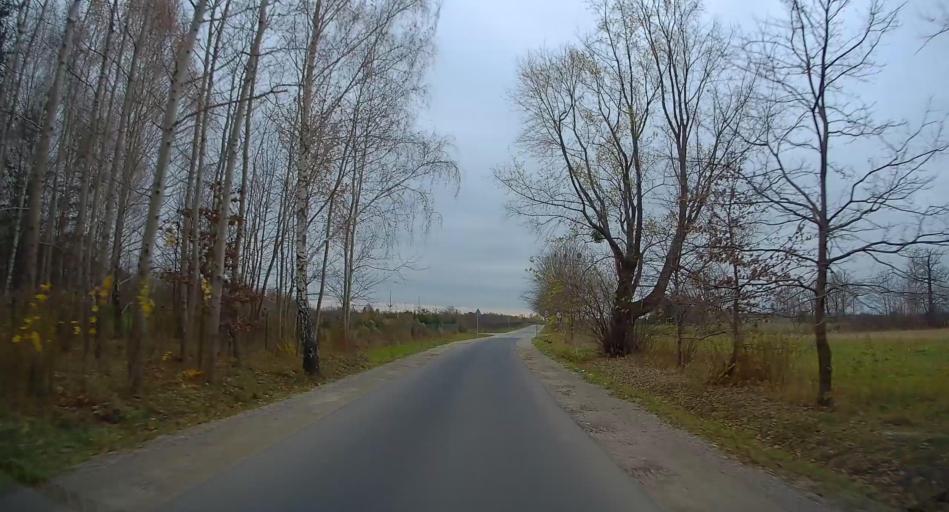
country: PL
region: Lodz Voivodeship
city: Zabia Wola
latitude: 52.0093
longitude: 20.6556
